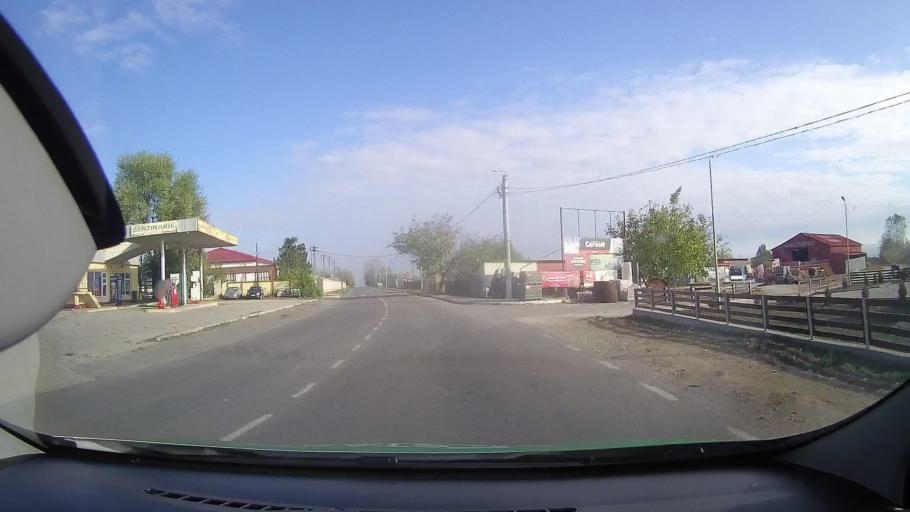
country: RO
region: Tulcea
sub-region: Comuna Mahmudia
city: Mahmudia
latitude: 45.0792
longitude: 29.0791
